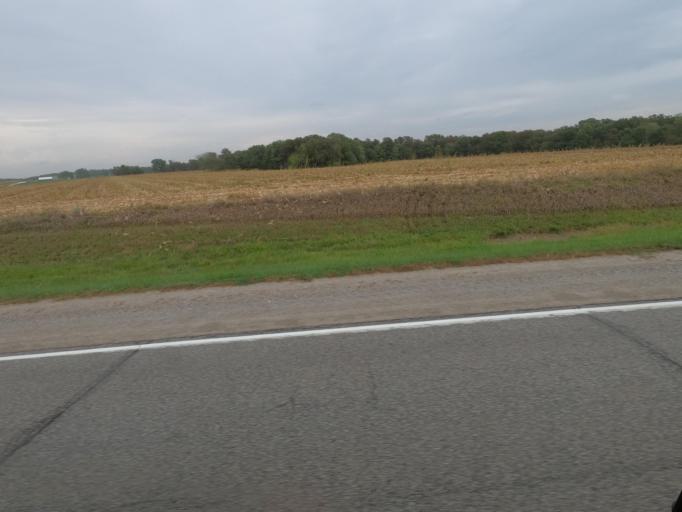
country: US
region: Iowa
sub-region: Van Buren County
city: Keosauqua
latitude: 40.8453
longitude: -92.0287
